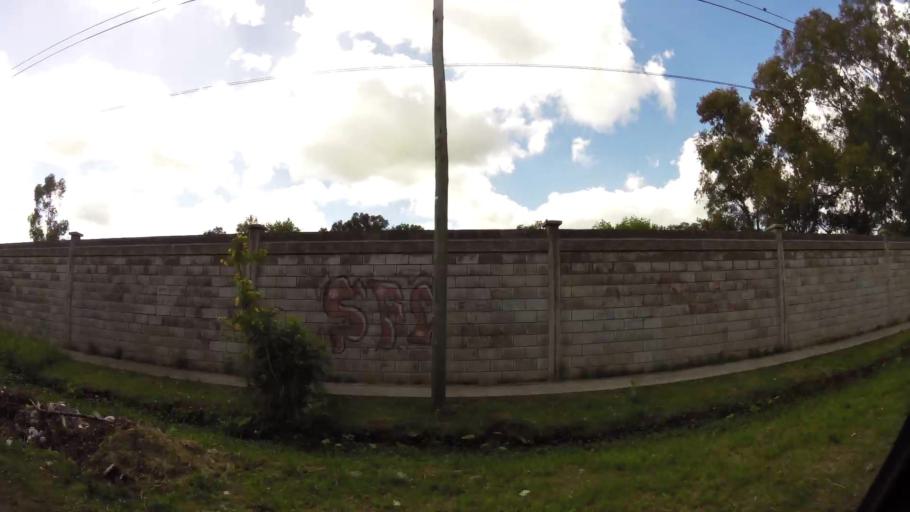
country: AR
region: Buenos Aires
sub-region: Partido de Quilmes
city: Quilmes
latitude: -34.8300
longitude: -58.1863
